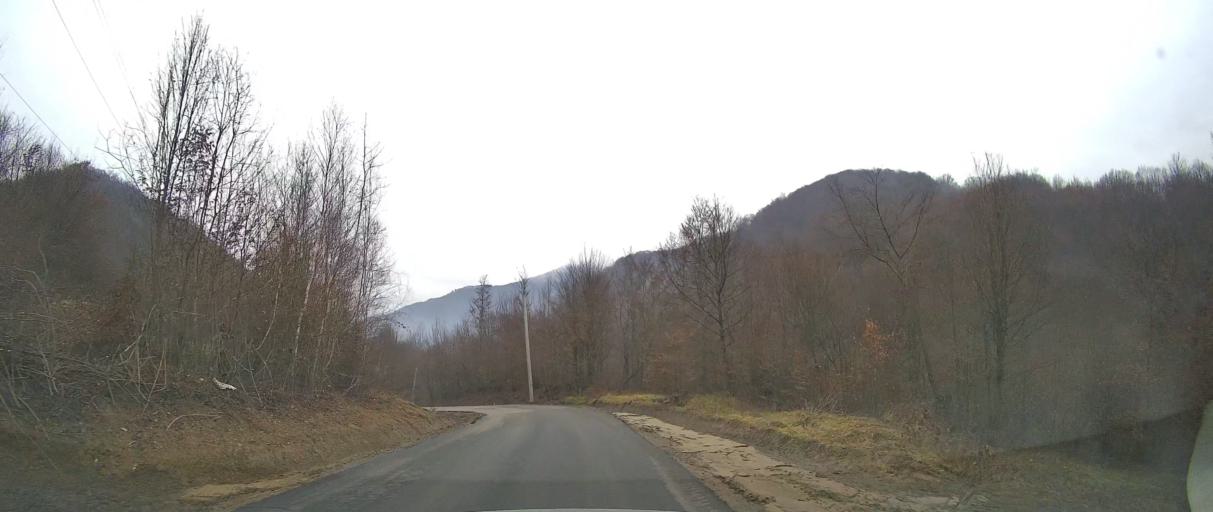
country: UA
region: Zakarpattia
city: Velykyi Bereznyi
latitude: 48.9558
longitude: 22.5462
